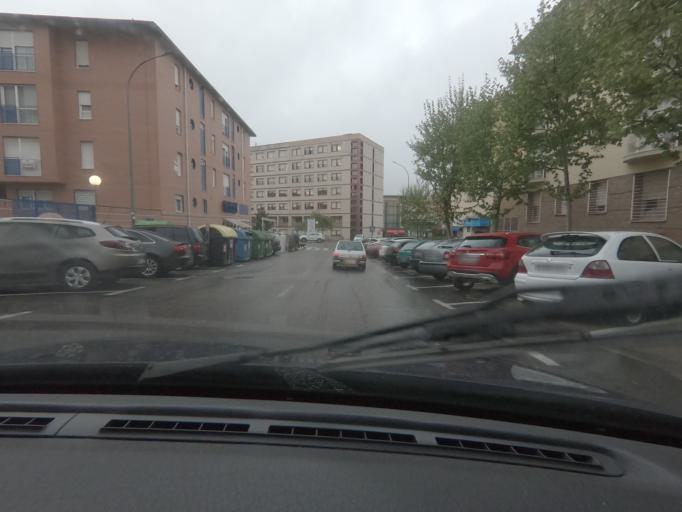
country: ES
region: Extremadura
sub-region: Provincia de Badajoz
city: Merida
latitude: 38.9115
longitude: -6.3629
